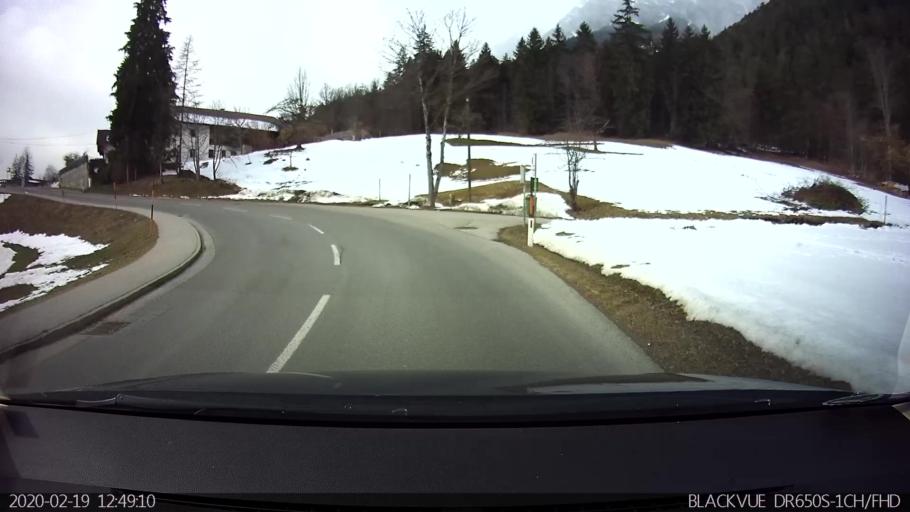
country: AT
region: Tyrol
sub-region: Politischer Bezirk Innsbruck Land
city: Gnadenwald
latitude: 47.3215
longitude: 11.5587
